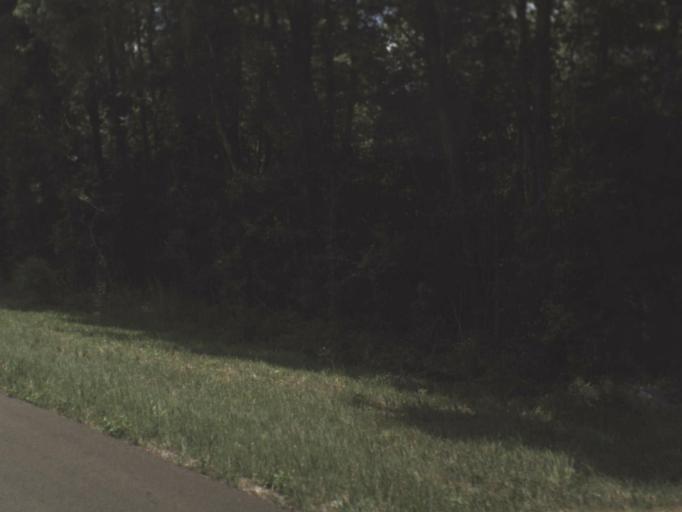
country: US
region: Florida
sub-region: Alachua County
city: Alachua
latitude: 29.7537
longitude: -82.3564
